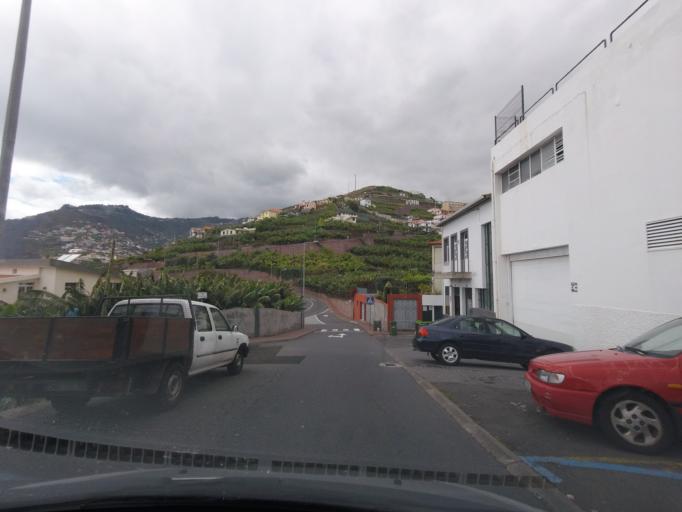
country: PT
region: Madeira
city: Camara de Lobos
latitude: 32.6478
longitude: -16.9709
